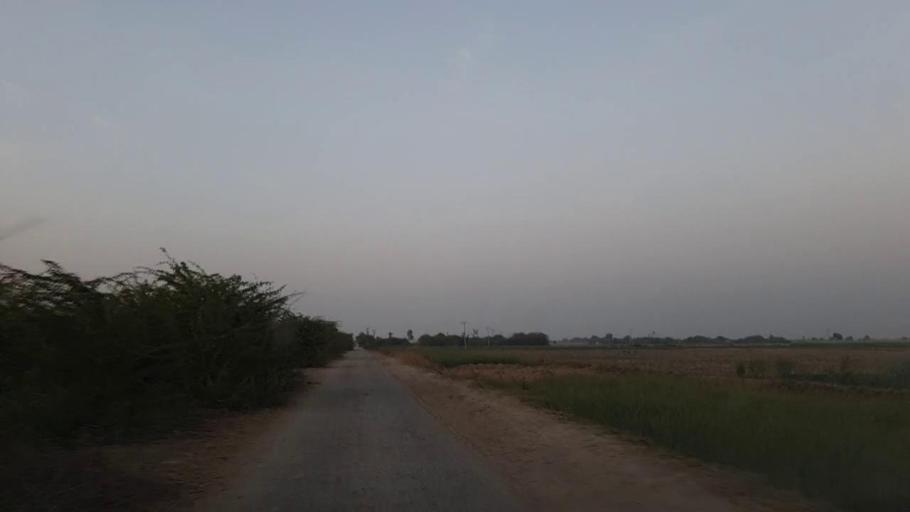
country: PK
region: Sindh
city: Naukot
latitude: 24.9933
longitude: 69.4245
